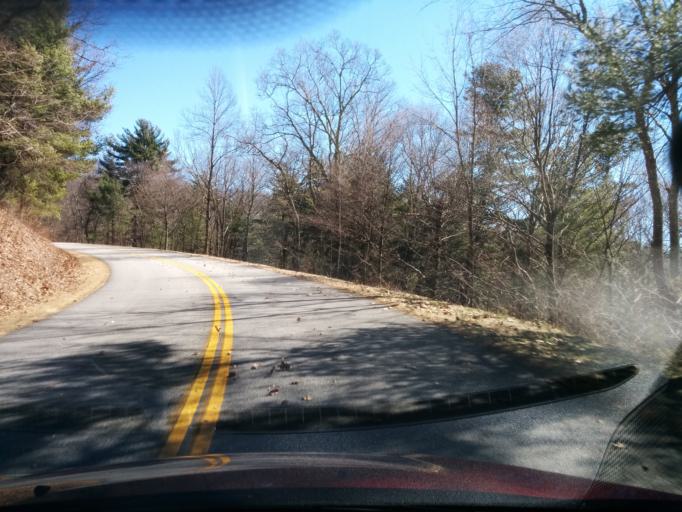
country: US
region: Virginia
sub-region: Augusta County
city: Stuarts Draft
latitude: 37.8777
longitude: -79.1534
